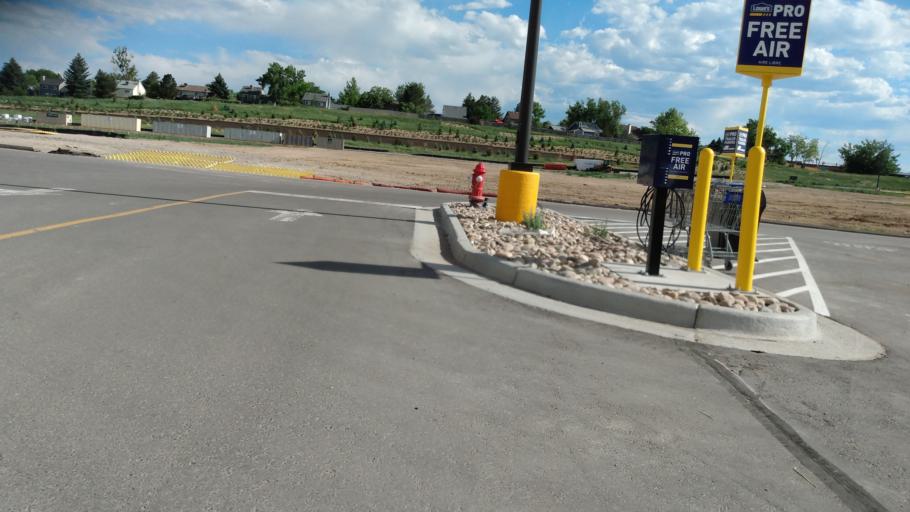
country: US
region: Colorado
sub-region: Boulder County
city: Lafayette
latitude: 40.0131
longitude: -105.1009
